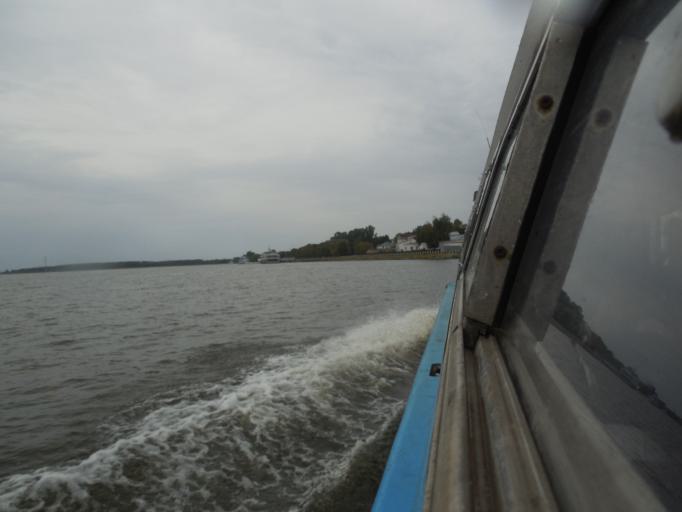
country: RU
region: Kostroma
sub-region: Kostromskoy Rayon
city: Kostroma
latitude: 57.7604
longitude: 40.9280
